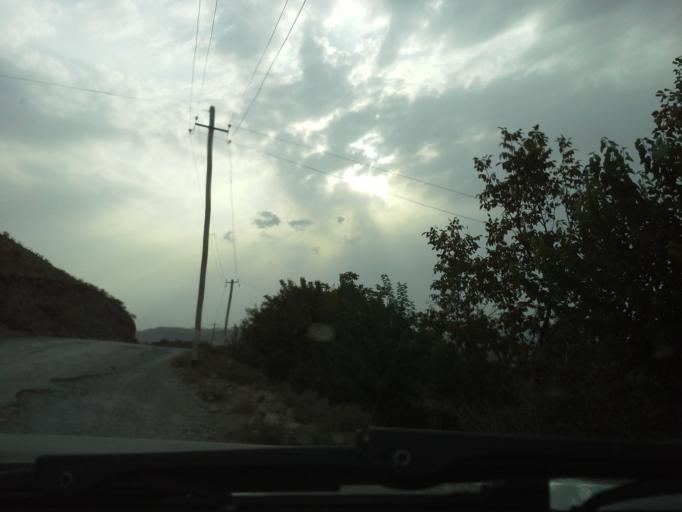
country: UZ
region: Qashqadaryo
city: Qorashina
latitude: 37.9234
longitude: 66.4905
